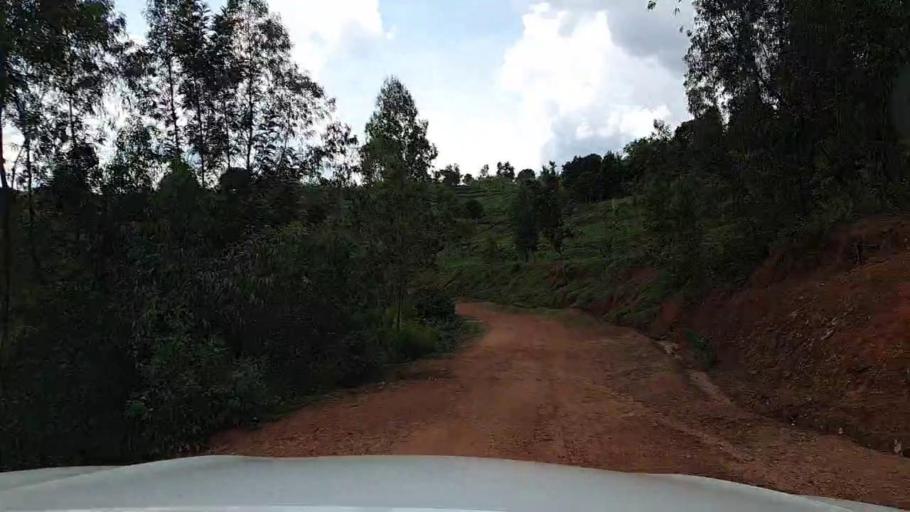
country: RW
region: Southern Province
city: Butare
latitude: -2.7558
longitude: 29.7480
